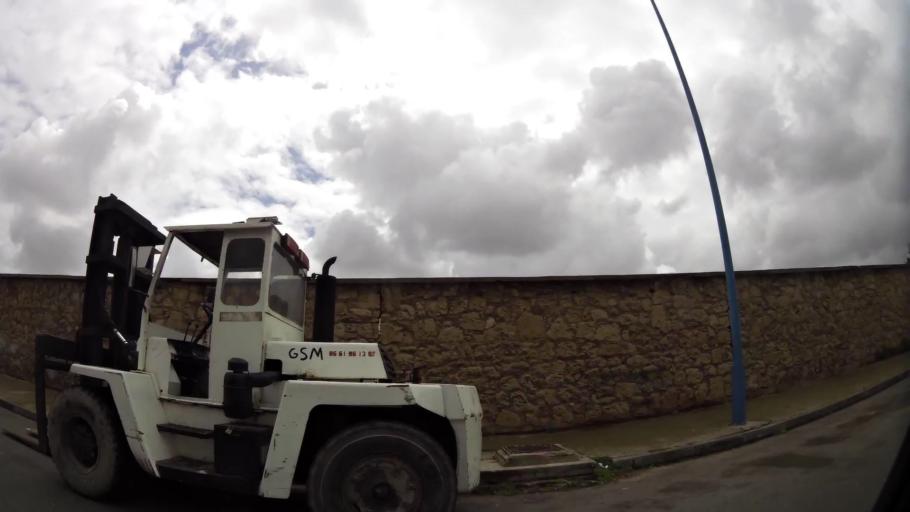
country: MA
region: Grand Casablanca
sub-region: Mediouna
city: Tit Mellil
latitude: 33.6108
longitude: -7.5235
